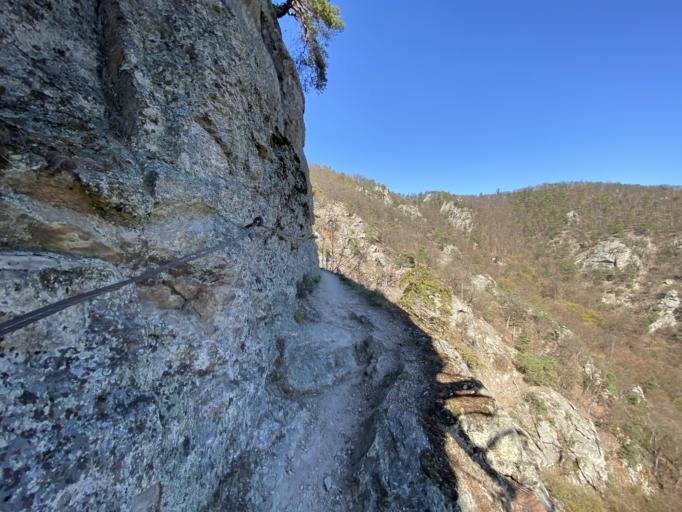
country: AT
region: Lower Austria
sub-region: Politischer Bezirk Krems
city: Durnstein
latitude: 48.4055
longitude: 15.5234
